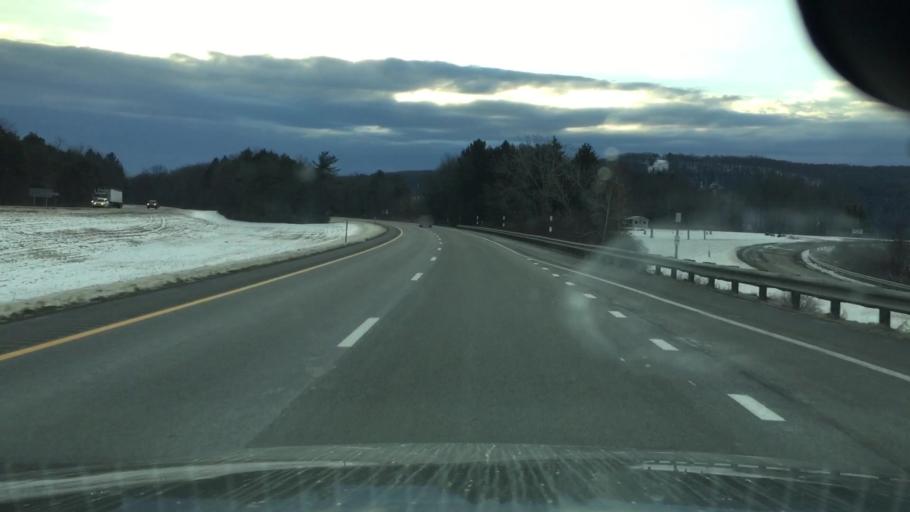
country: US
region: Pennsylvania
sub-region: Bradford County
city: South Waverly
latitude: 42.0025
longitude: -76.6224
